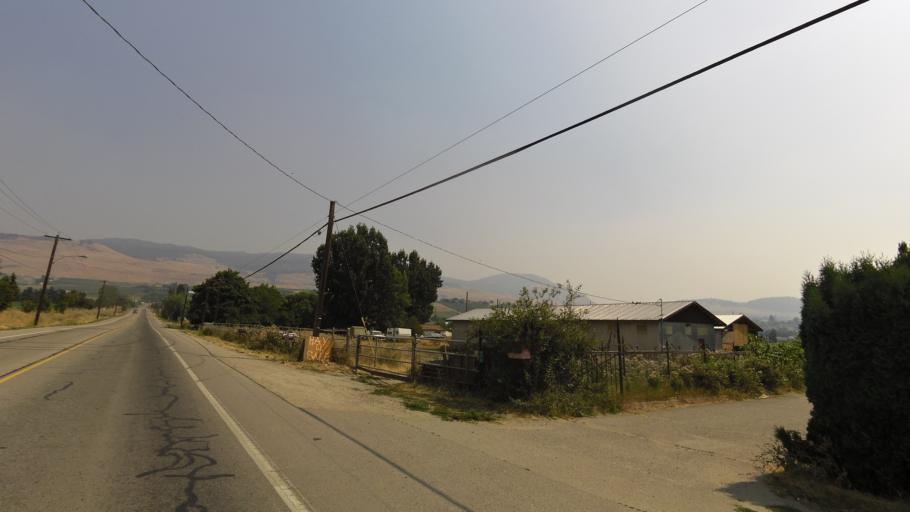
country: CA
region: British Columbia
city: Kelowna
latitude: 49.9181
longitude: -119.3791
